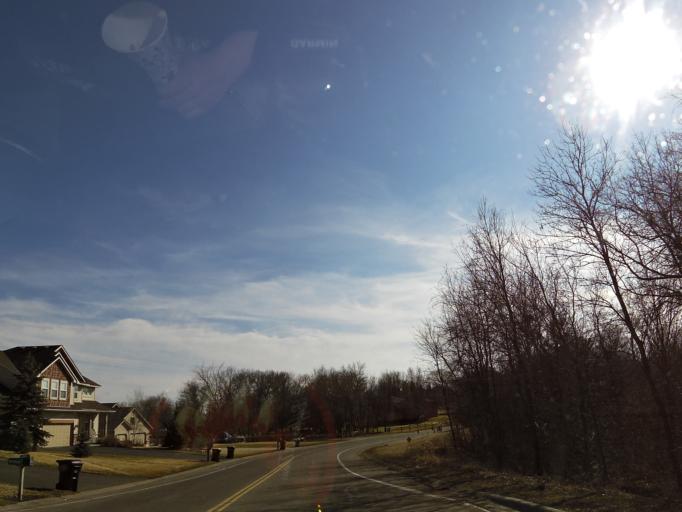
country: US
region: Minnesota
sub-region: Scott County
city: Prior Lake
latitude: 44.7237
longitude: -93.4484
